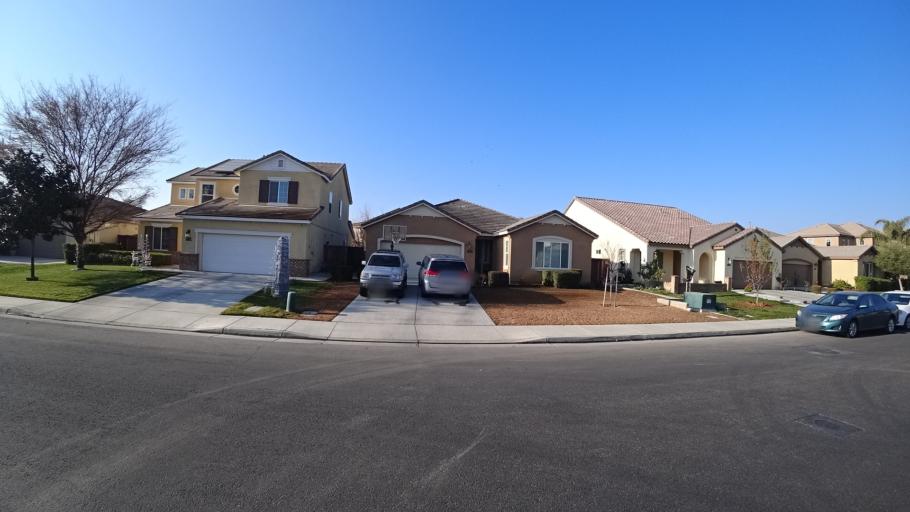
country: US
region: California
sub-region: Kern County
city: Greenacres
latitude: 35.3017
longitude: -119.1155
